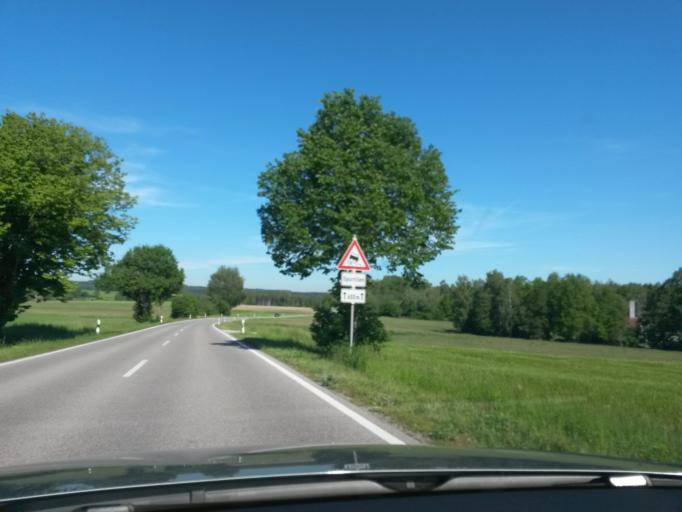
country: DE
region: Baden-Wuerttemberg
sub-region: Tuebingen Region
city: Durnau
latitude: 48.0630
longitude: 9.5822
